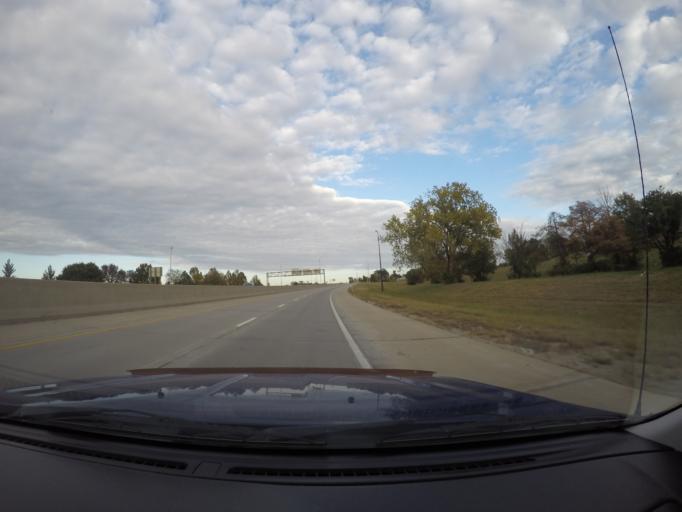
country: US
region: Kansas
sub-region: Shawnee County
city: Topeka
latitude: 39.0671
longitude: -95.7299
